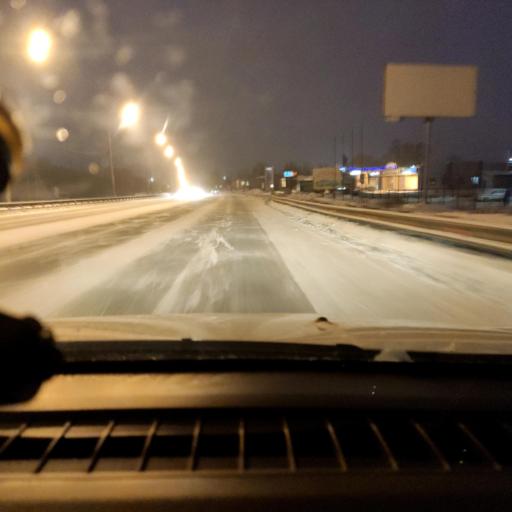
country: RU
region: Samara
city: Otradnyy
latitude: 53.3704
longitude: 51.3654
